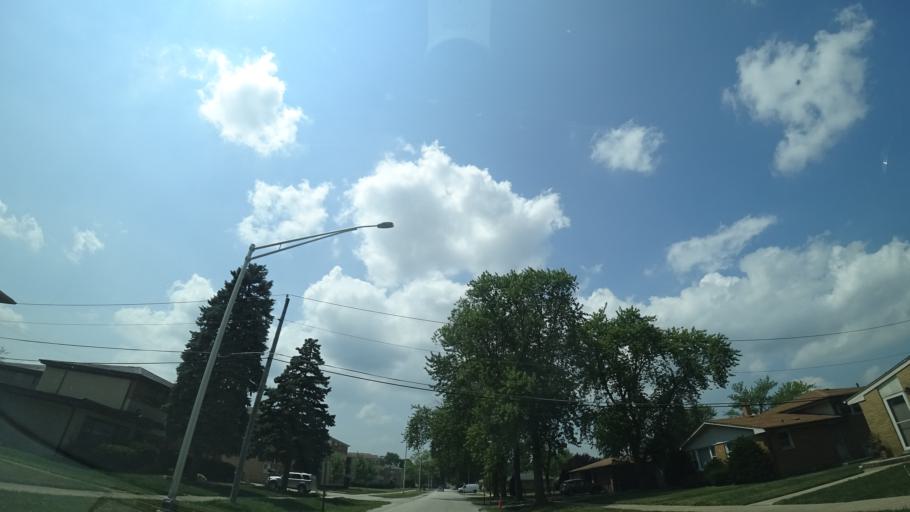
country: US
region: Illinois
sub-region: Cook County
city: Chicago Ridge
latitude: 41.6916
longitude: -87.7853
